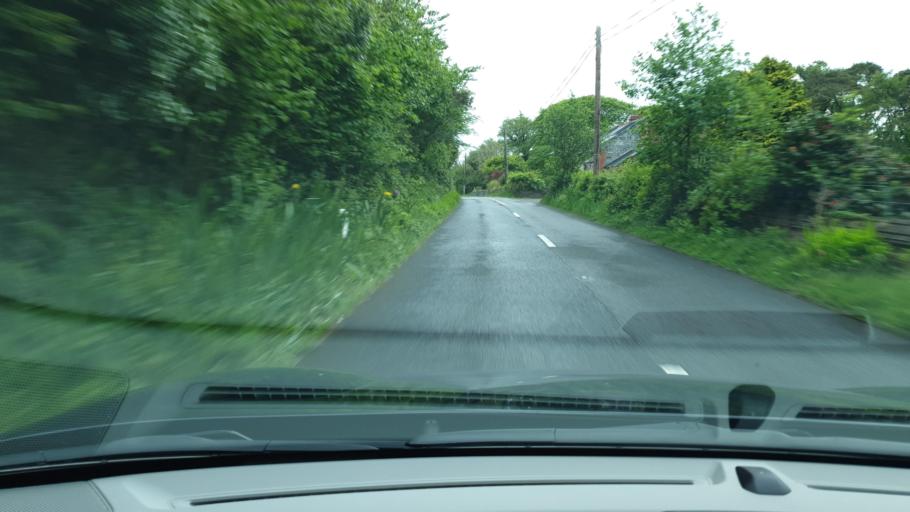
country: IE
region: Connaught
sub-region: County Galway
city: Clifden
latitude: 53.4554
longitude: -9.8666
